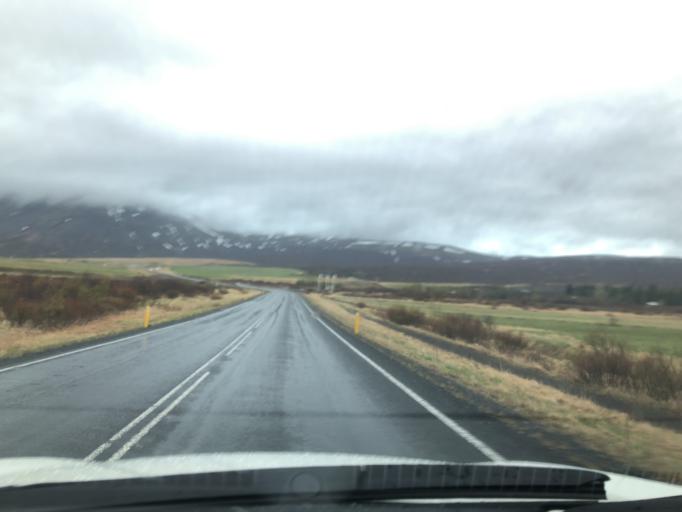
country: IS
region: South
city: Selfoss
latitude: 64.2397
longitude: -20.6613
